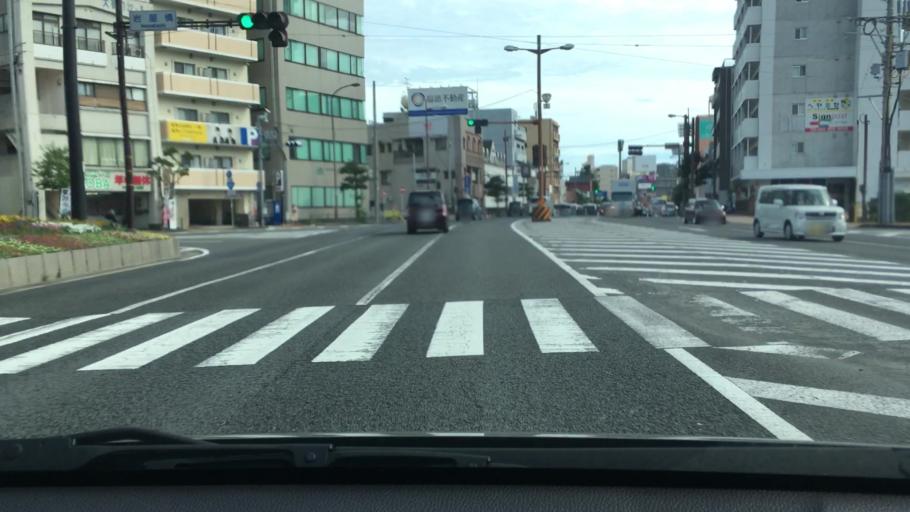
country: JP
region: Nagasaki
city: Nagasaki-shi
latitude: 32.7815
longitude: 129.8624
